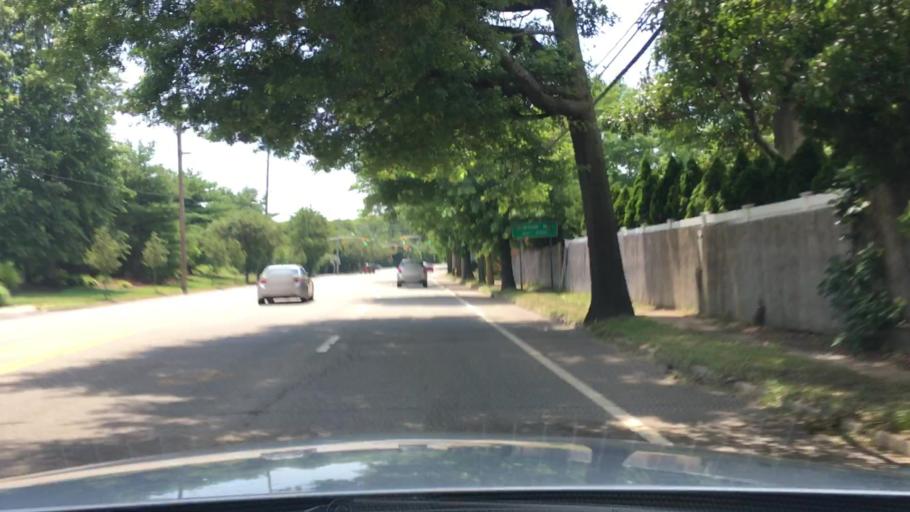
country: US
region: New York
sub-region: Nassau County
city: Woodbury
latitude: 40.8024
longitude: -73.4815
